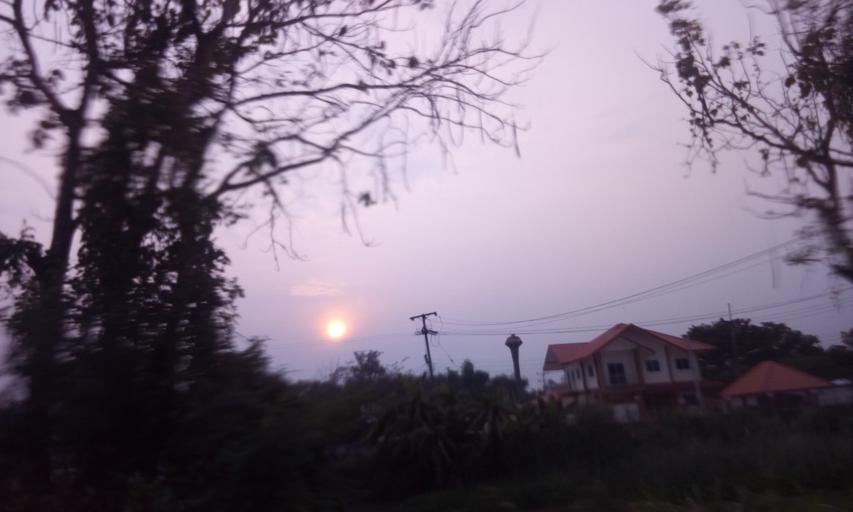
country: TH
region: Bangkok
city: Nong Chok
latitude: 13.9575
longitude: 100.8952
